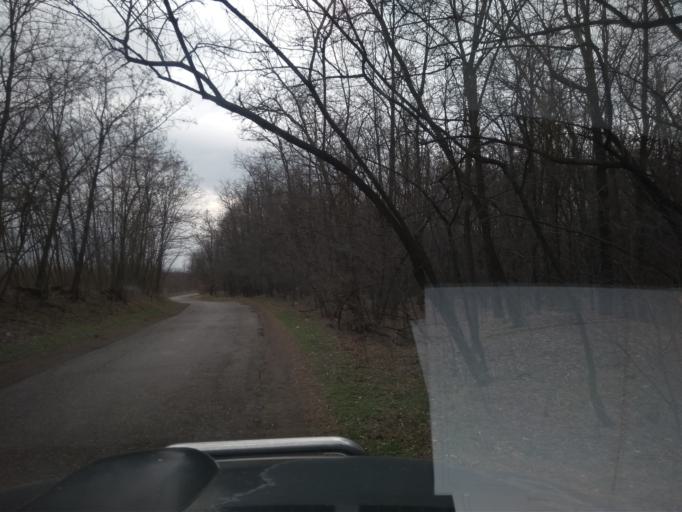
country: HU
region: Szabolcs-Szatmar-Bereg
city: Nyirpazony
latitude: 48.0176
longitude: 21.8081
